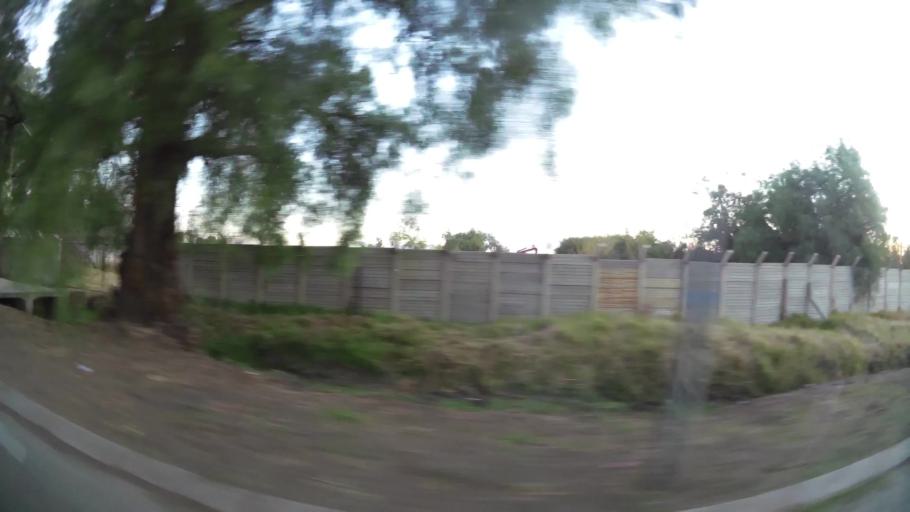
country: ZA
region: Northern Cape
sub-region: Frances Baard District Municipality
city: Kimberley
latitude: -28.7231
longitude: 24.7747
